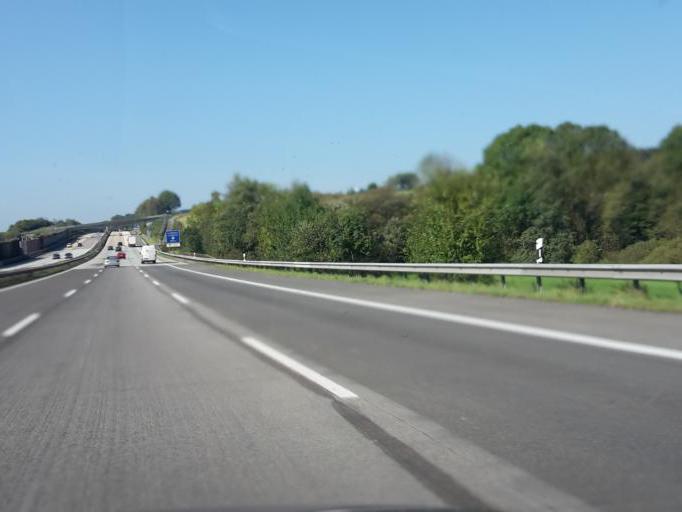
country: DE
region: Rheinland-Pfalz
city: Oberhaid
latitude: 50.5097
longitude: 7.7085
